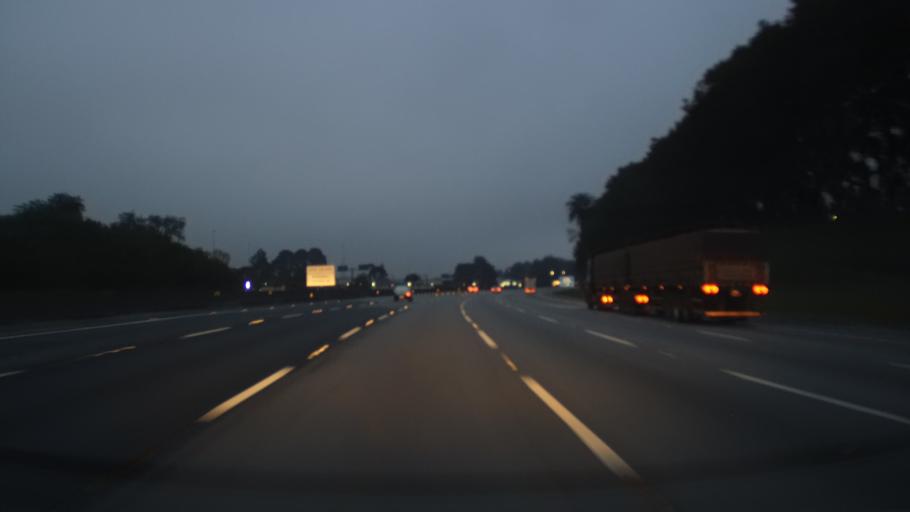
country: BR
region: Sao Paulo
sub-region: Sao Bernardo Do Campo
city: Sao Bernardo do Campo
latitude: -23.7869
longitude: -46.5961
